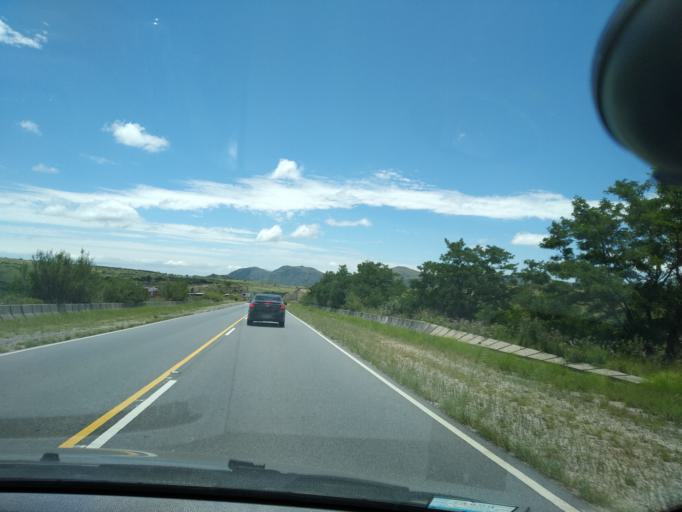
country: AR
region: Cordoba
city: Cuesta Blanca
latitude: -31.5807
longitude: -64.6086
